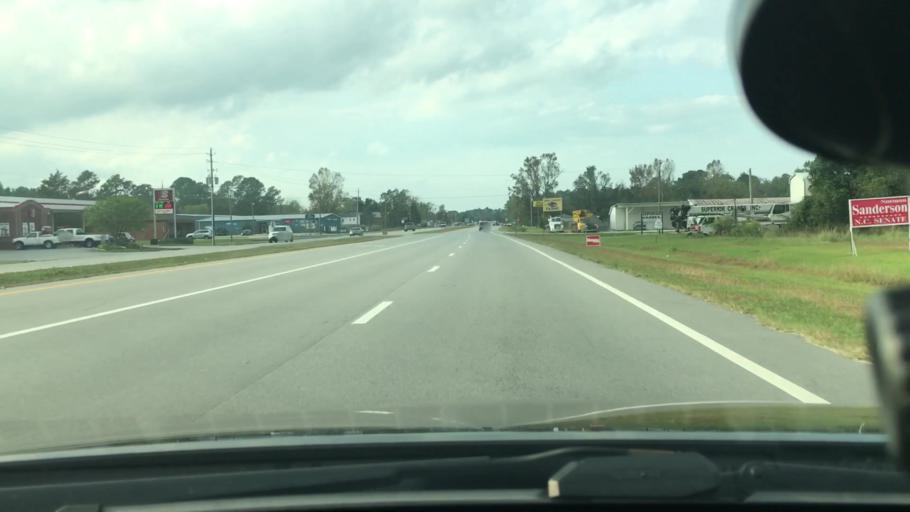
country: US
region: North Carolina
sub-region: Craven County
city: New Bern
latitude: 35.1216
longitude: -77.0186
